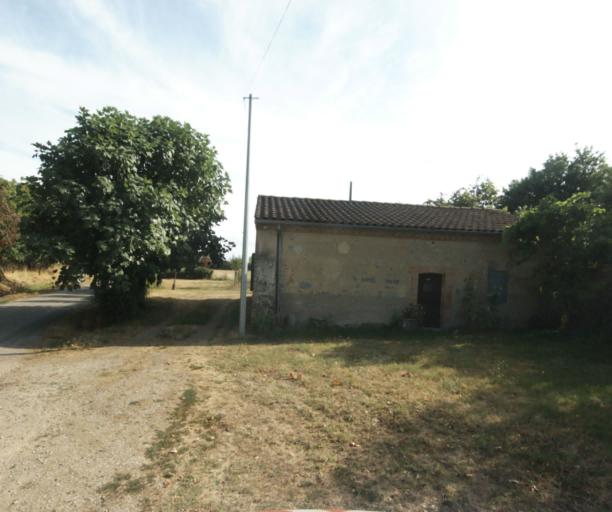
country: FR
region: Midi-Pyrenees
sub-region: Departement de la Haute-Garonne
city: Revel
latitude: 43.5012
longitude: 1.9957
